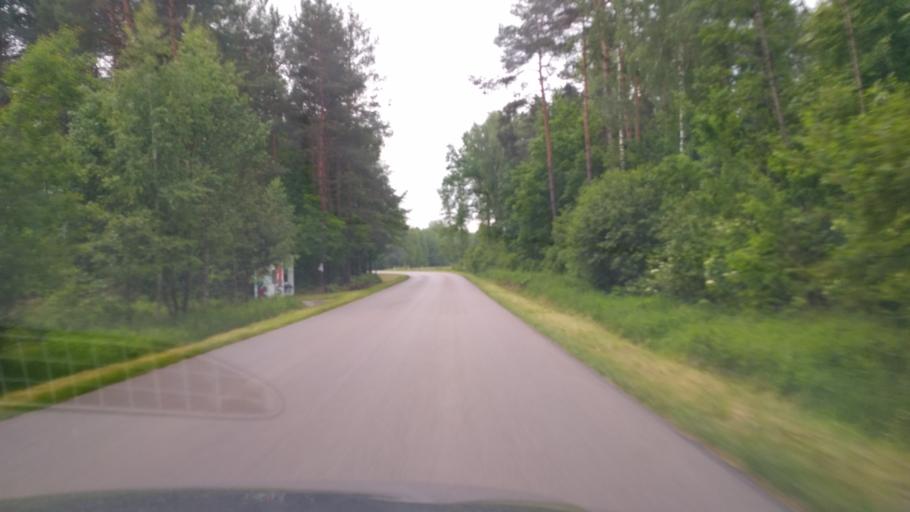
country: PL
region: Subcarpathian Voivodeship
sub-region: Powiat kolbuszowski
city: Niwiska
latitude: 50.1839
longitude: 21.6570
